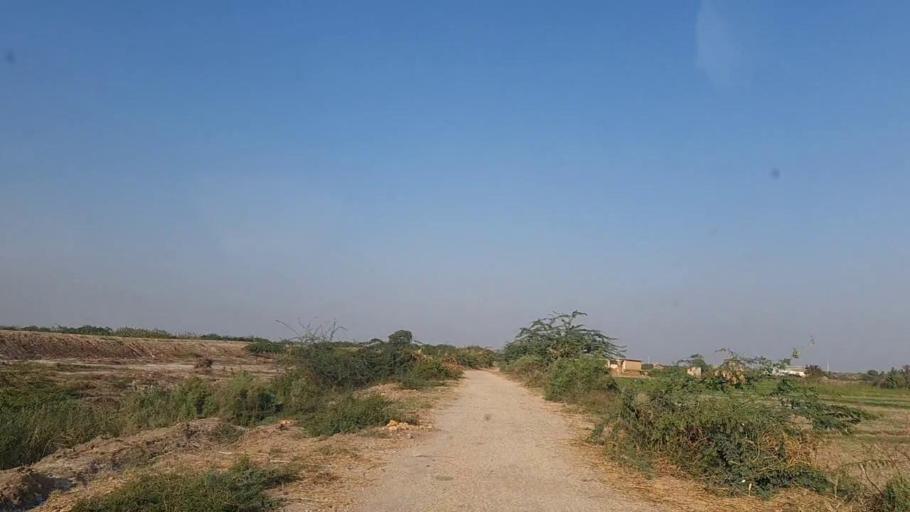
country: PK
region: Sindh
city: Thatta
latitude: 24.7244
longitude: 67.9479
